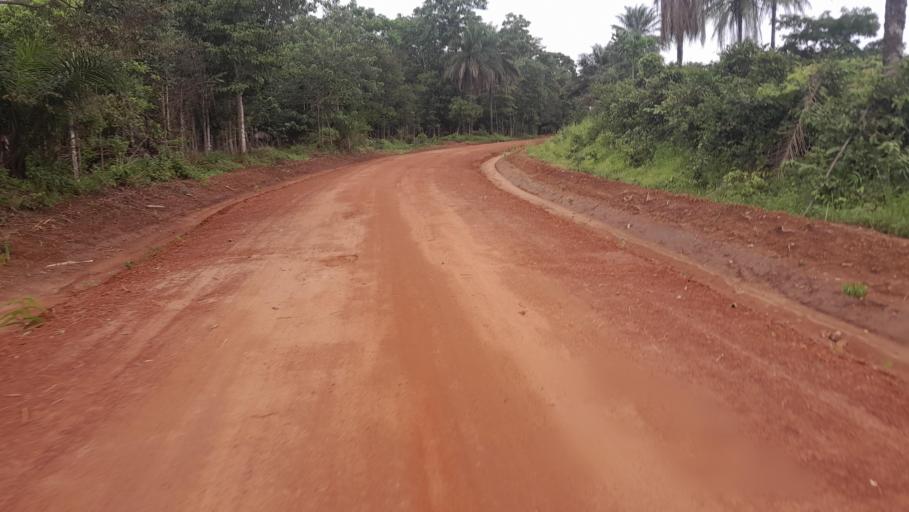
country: GN
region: Boke
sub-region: Boffa
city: Boffa
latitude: 10.0547
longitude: -13.8714
